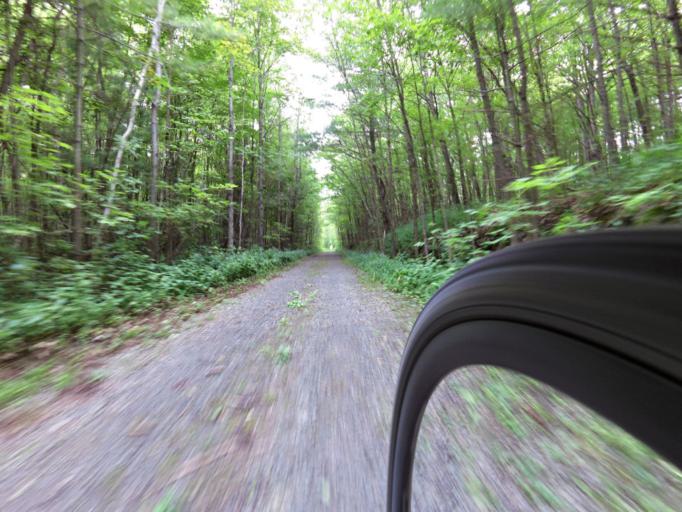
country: CA
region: Ontario
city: Gananoque
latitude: 44.5902
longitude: -76.3066
